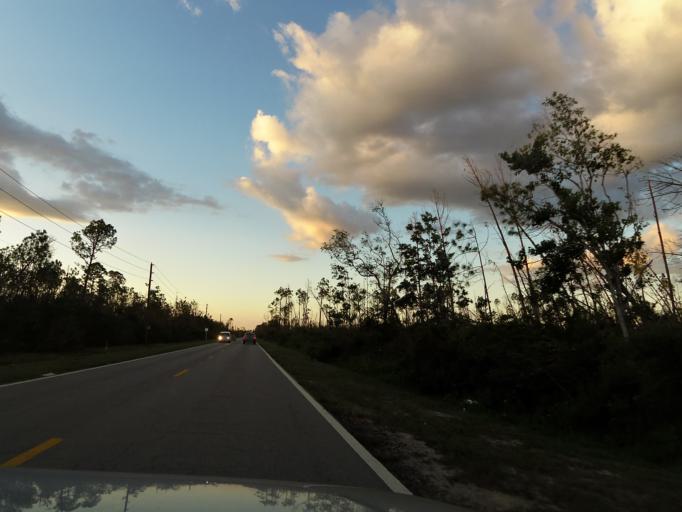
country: US
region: Florida
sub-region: Bay County
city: Mexico Beach
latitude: 29.9329
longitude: -85.3885
